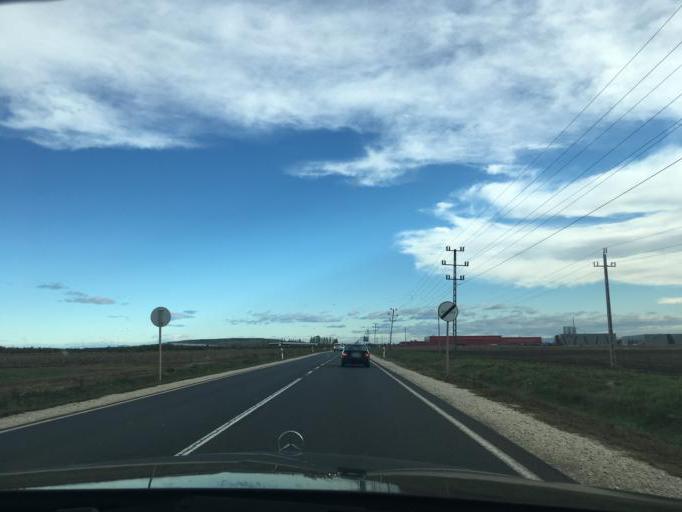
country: HU
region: Borsod-Abauj-Zemplen
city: Szikszo
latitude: 48.1688
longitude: 20.9097
